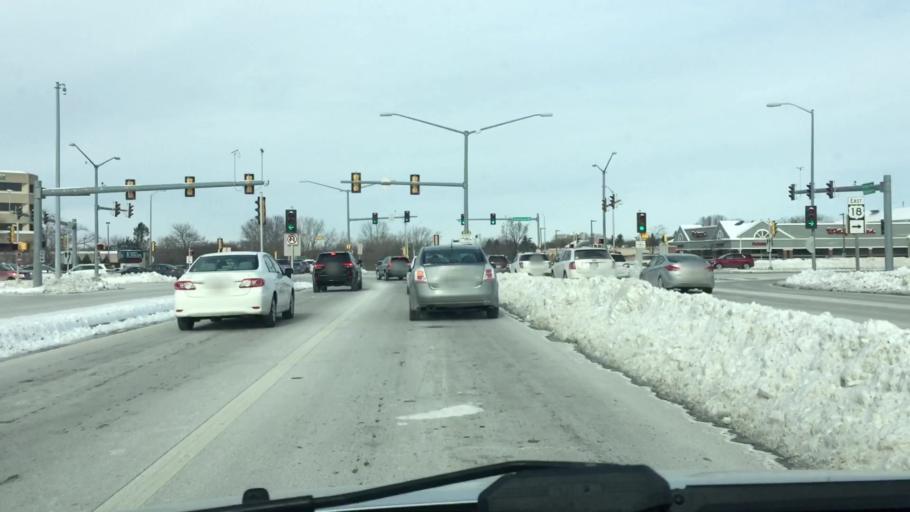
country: US
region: Wisconsin
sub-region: Waukesha County
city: Brookfield
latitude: 43.0353
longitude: -88.1068
